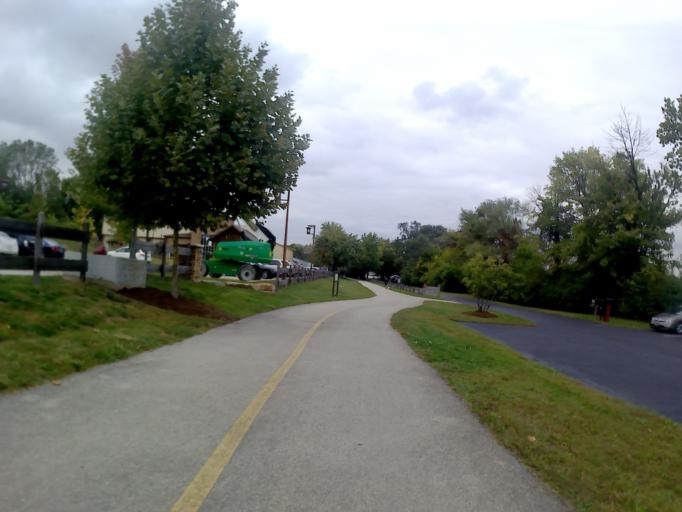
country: US
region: Illinois
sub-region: Kane County
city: Aurora
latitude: 41.7713
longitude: -88.3109
